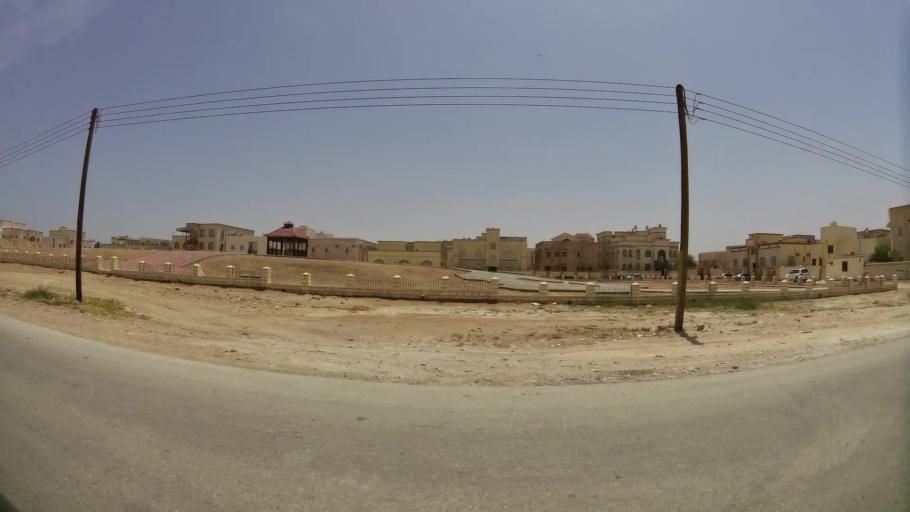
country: OM
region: Zufar
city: Salalah
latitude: 17.0577
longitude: 54.1617
